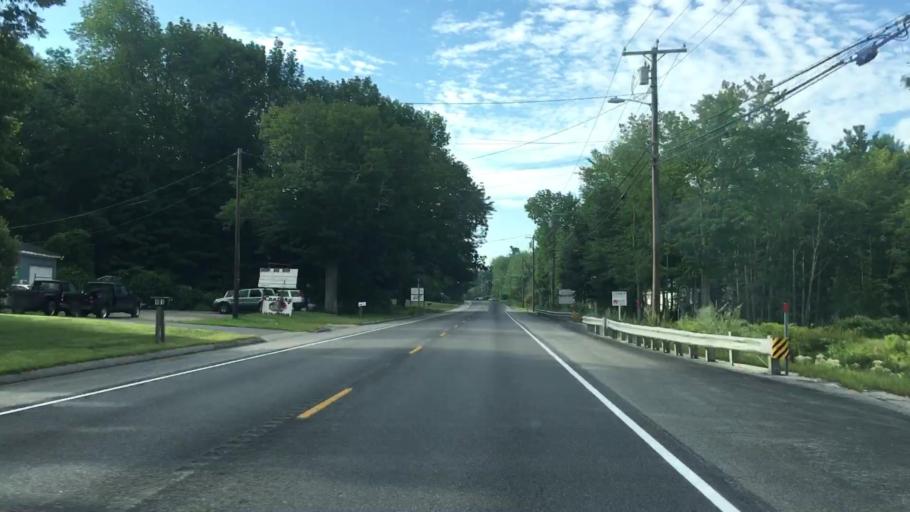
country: US
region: Maine
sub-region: Cumberland County
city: South Windham
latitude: 43.7708
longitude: -70.3789
